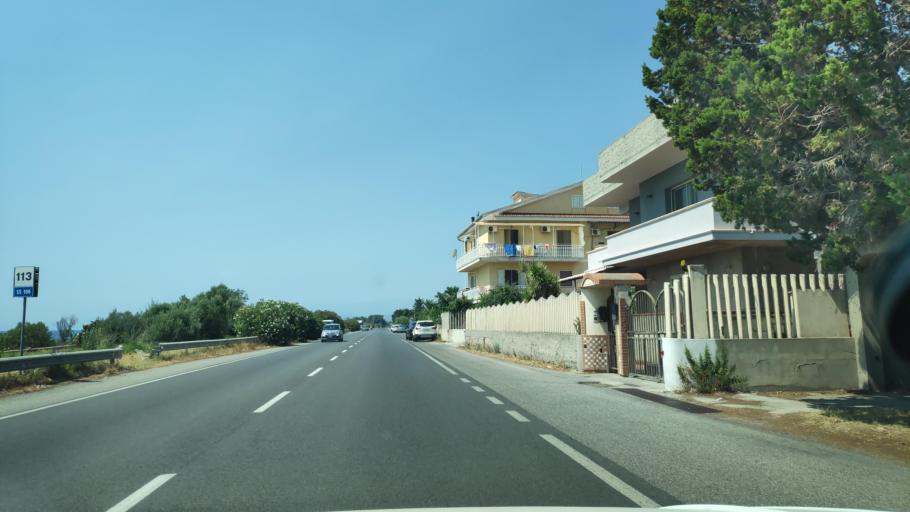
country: IT
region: Calabria
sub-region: Provincia di Reggio Calabria
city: Roccella Ionica
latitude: 38.3134
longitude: 16.3807
